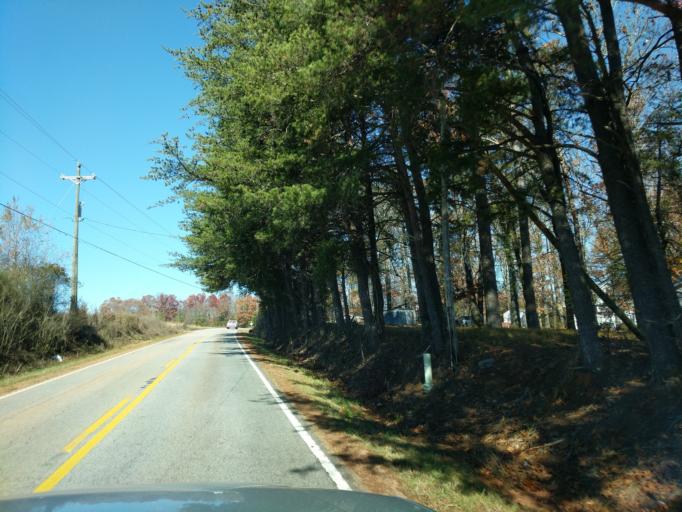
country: US
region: South Carolina
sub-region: Spartanburg County
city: Inman Mills
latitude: 35.0306
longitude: -82.1849
